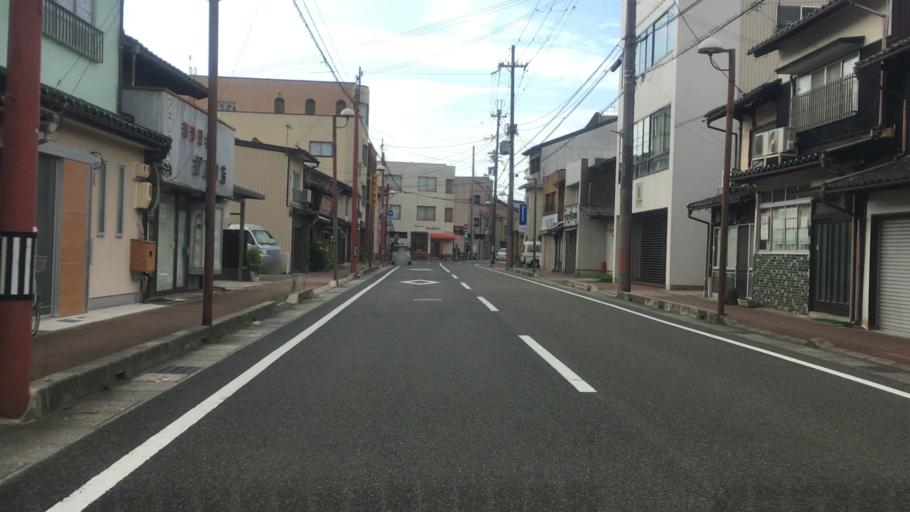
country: JP
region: Hyogo
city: Toyooka
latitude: 35.5392
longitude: 134.8235
